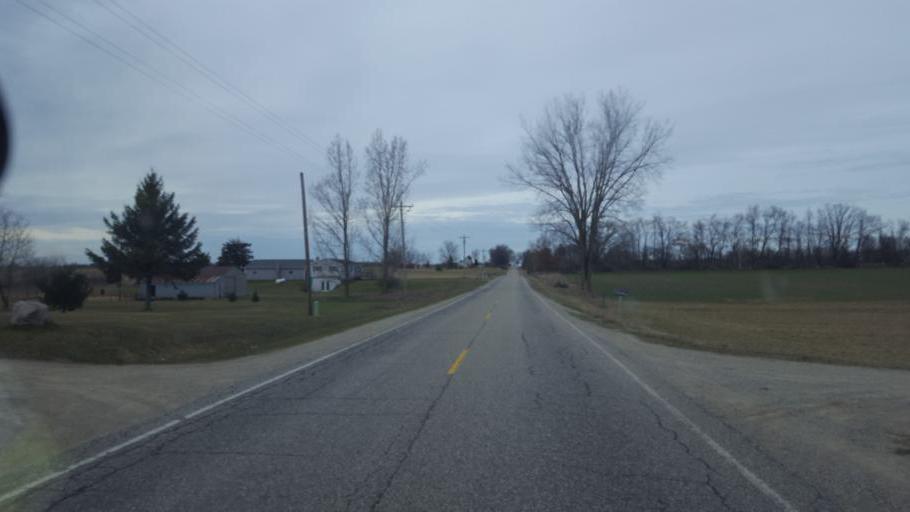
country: US
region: Michigan
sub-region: Montcalm County
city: Edmore
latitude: 43.4601
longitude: -85.0052
